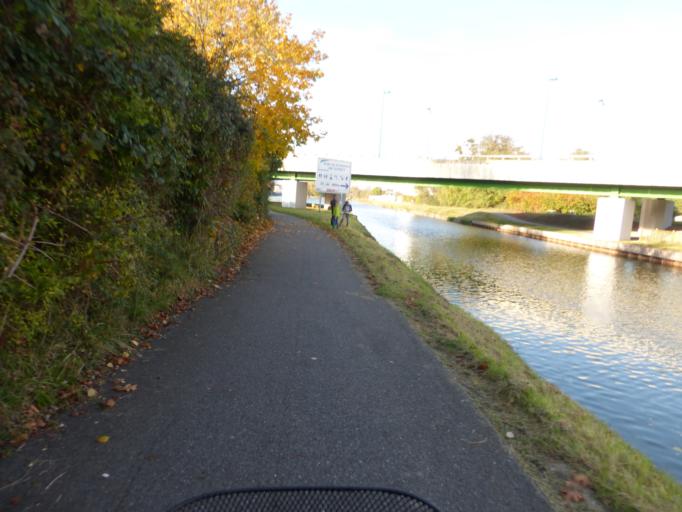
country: FR
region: Lorraine
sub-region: Departement de Meurthe-et-Moselle
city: Jarville-la-Malgrange
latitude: 48.6778
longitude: 6.2015
